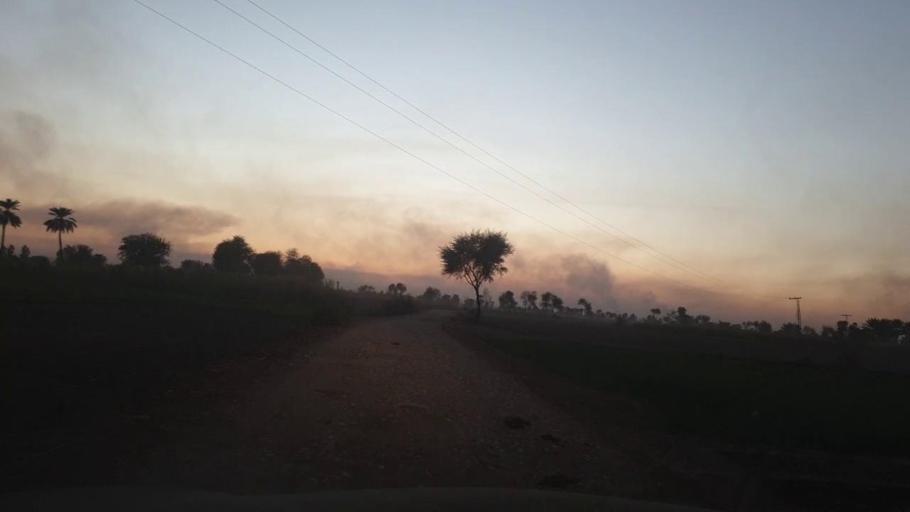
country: PK
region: Sindh
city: Ghotki
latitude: 28.0358
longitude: 69.3485
